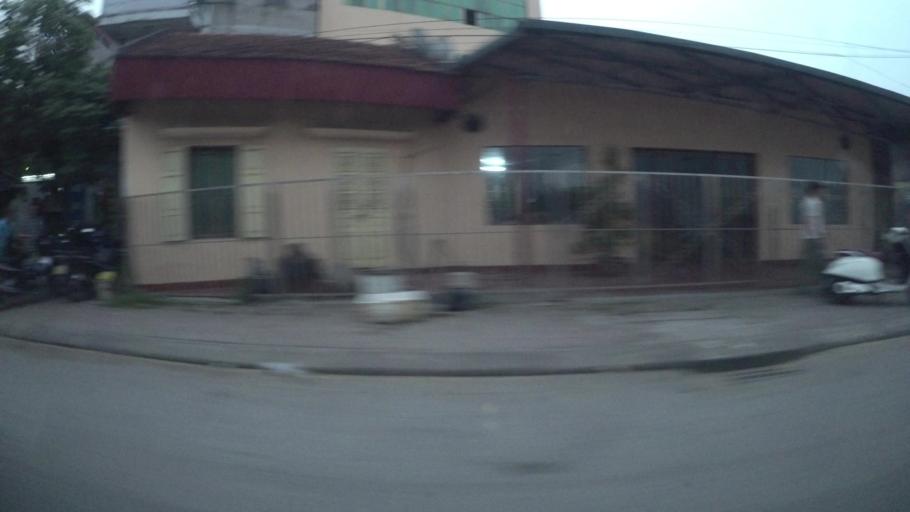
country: VN
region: Ha Noi
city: Trau Quy
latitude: 21.0411
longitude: 105.8976
